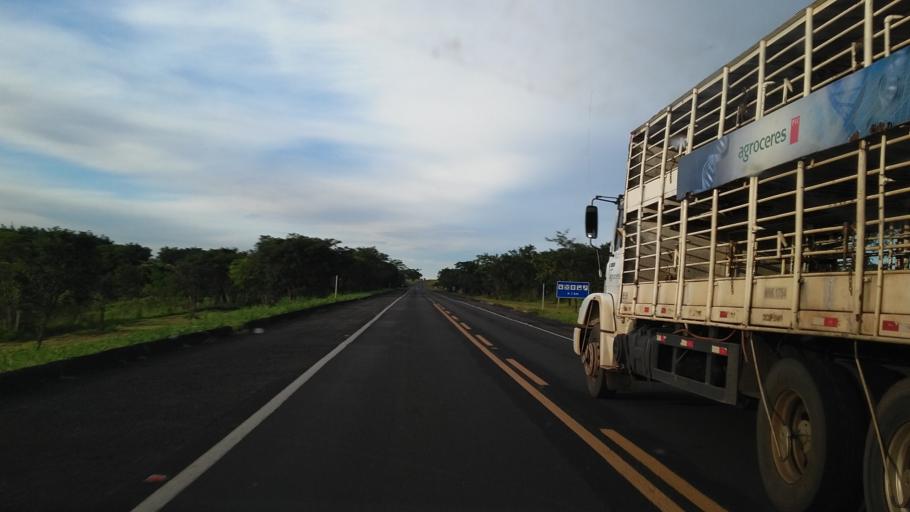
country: BR
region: Sao Paulo
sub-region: Marilia
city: Marilia
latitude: -21.9255
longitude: -49.9175
